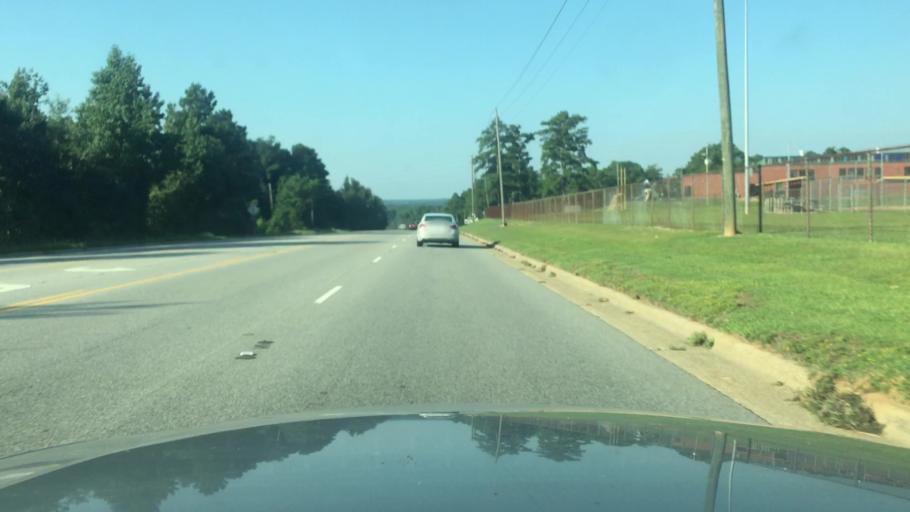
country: US
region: North Carolina
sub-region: Cumberland County
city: Eastover
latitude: 35.1813
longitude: -78.8550
